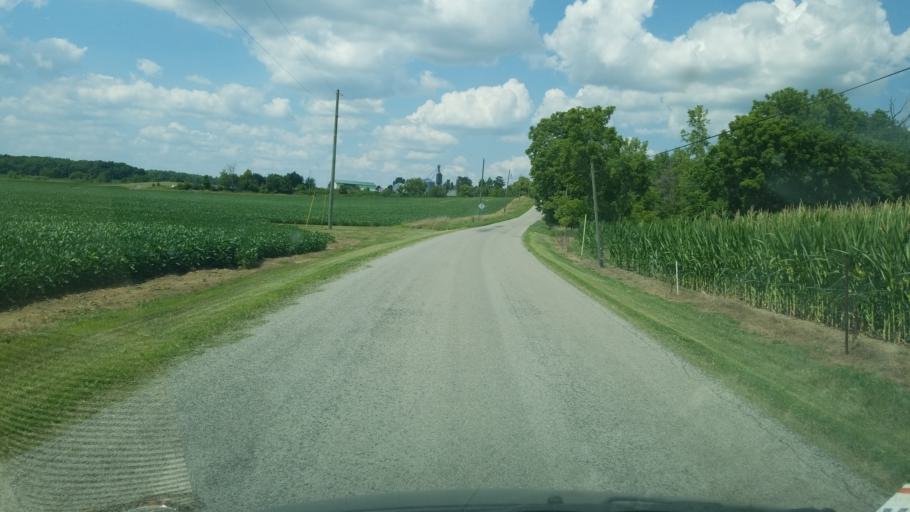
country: US
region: Ohio
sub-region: Champaign County
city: North Lewisburg
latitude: 40.2223
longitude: -83.4946
